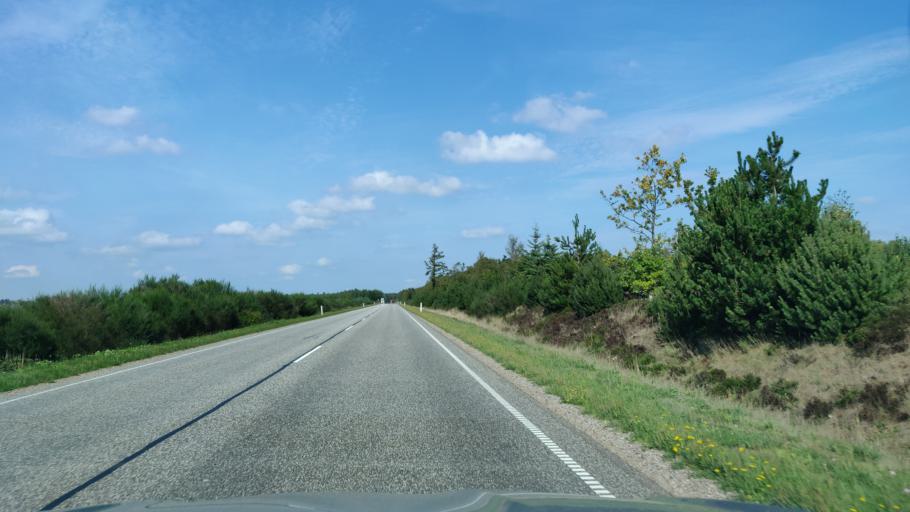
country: DK
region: Central Jutland
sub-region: Herning Kommune
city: Sunds
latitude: 56.3445
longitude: 8.9776
